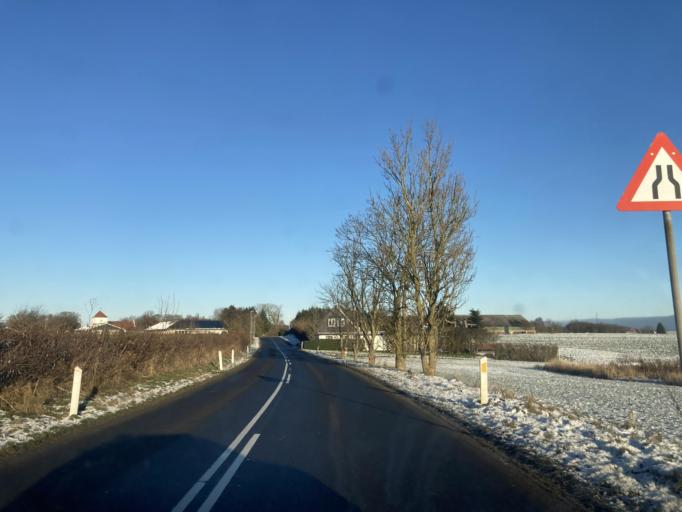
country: DK
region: South Denmark
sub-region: Svendborg Kommune
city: Thuro By
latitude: 55.1464
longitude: 10.7063
